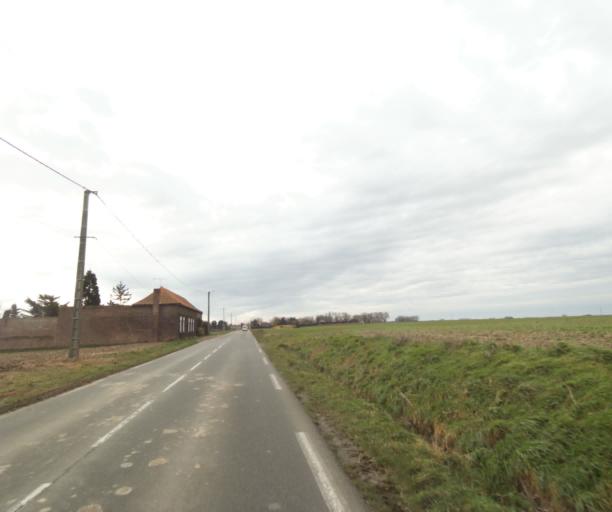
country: FR
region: Nord-Pas-de-Calais
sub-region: Departement du Nord
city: Sebourg
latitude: 50.3568
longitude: 3.6414
